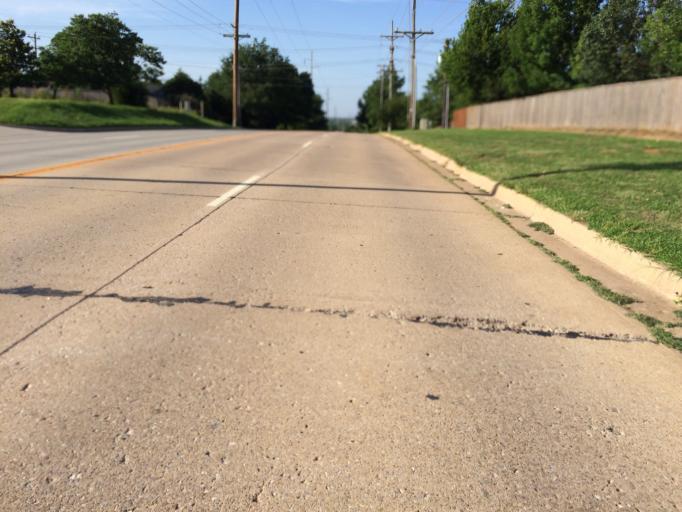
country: US
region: Oklahoma
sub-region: Cleveland County
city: Norman
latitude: 35.2118
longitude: -97.4943
